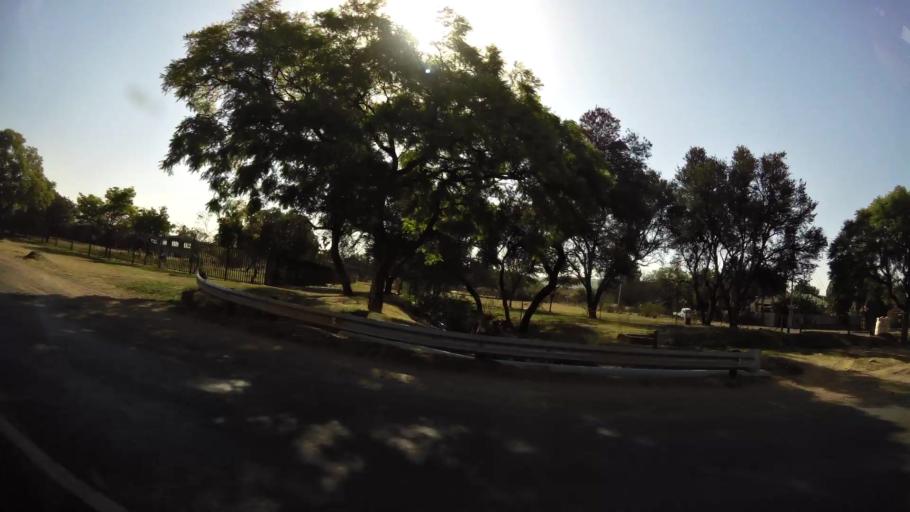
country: ZA
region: Gauteng
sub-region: City of Tshwane Metropolitan Municipality
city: Pretoria
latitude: -25.7173
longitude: 28.2455
